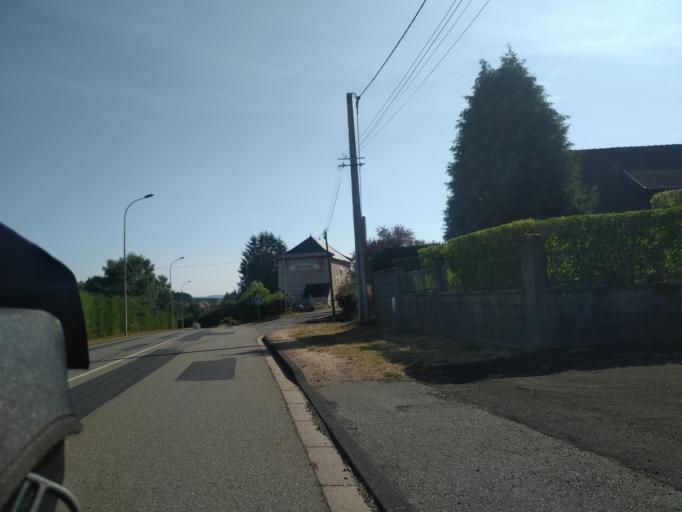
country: FR
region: Auvergne
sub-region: Departement du Puy-de-Dome
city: Saint-Georges-de-Mons
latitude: 45.9381
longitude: 2.8369
